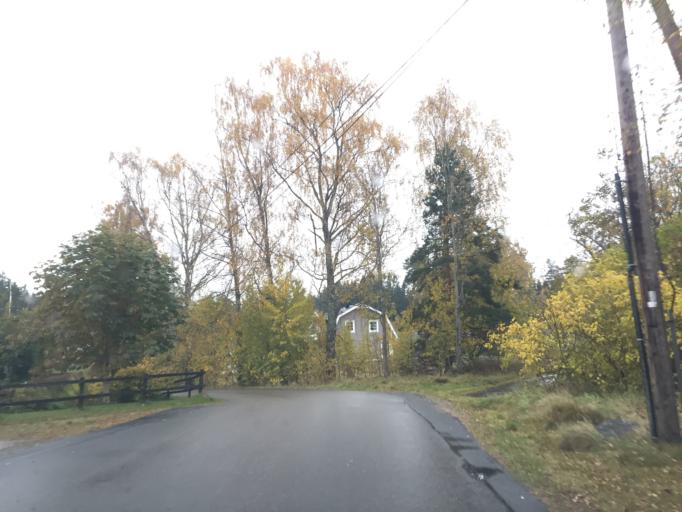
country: SE
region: Vaestra Goetaland
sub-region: Trollhattan
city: Trollhattan
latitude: 58.2855
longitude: 12.3383
